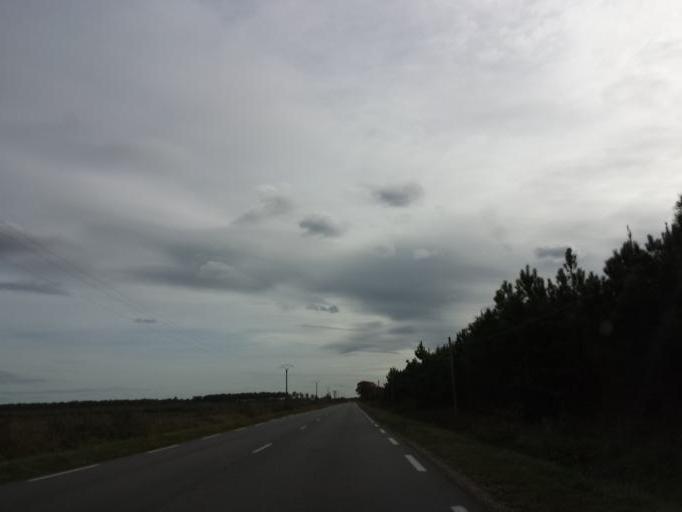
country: FR
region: Aquitaine
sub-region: Departement de la Gironde
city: Marcheprime
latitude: 44.7693
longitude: -0.9257
